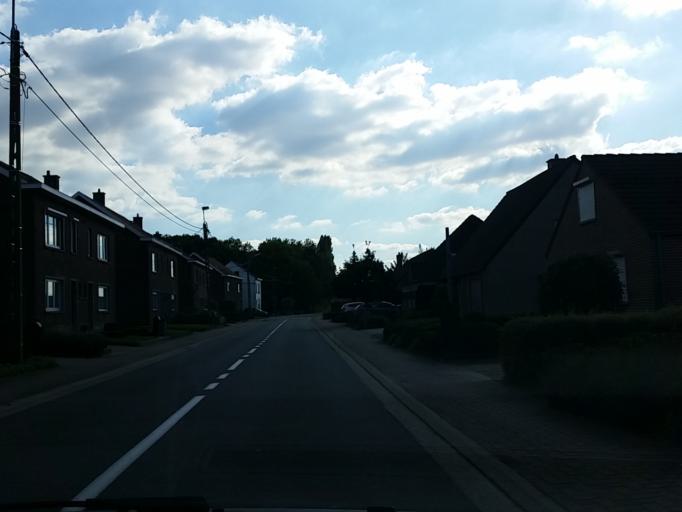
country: BE
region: Flanders
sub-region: Provincie Vlaams-Brabant
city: Herent
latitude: 50.9156
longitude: 4.6662
